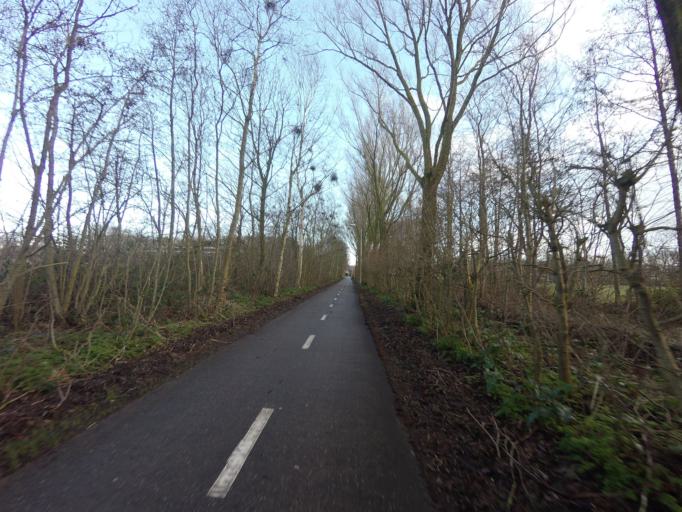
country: NL
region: North Holland
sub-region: Gemeente Texel
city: Den Burg
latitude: 53.1560
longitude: 4.8650
